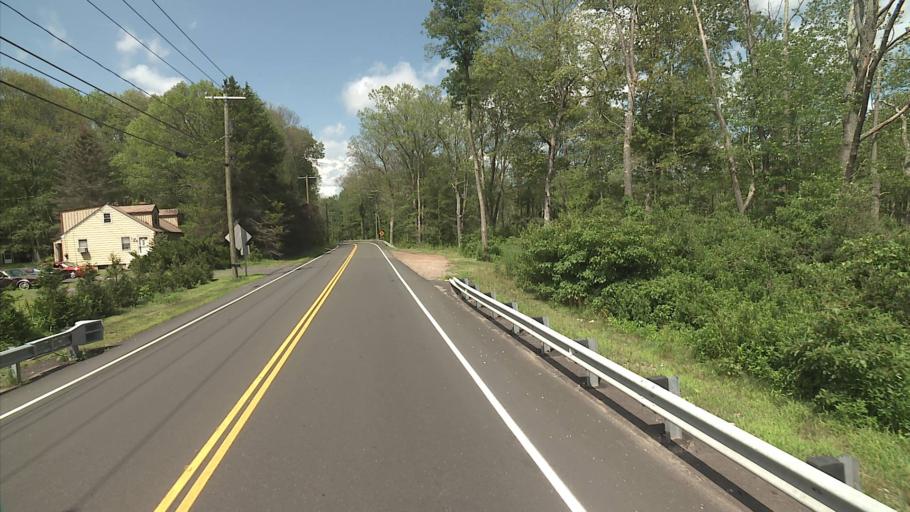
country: US
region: Connecticut
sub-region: Middlesex County
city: Higganum
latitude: 41.4054
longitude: -72.5621
